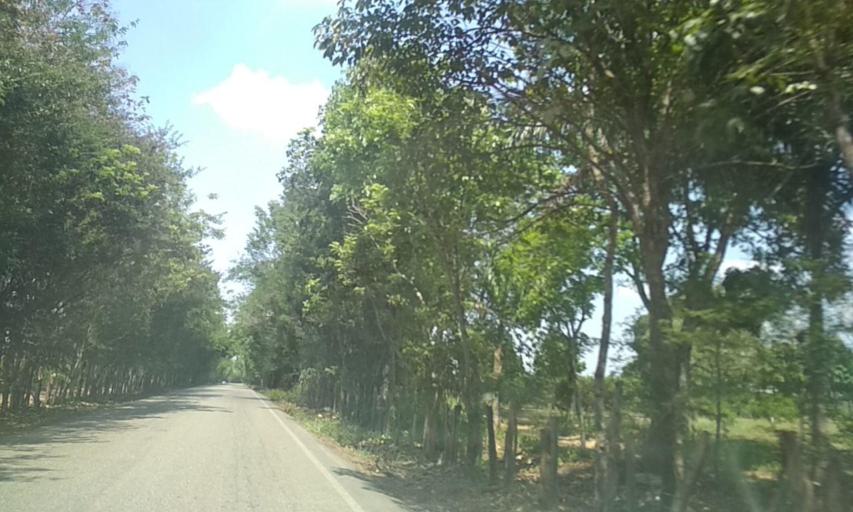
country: MX
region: Tabasco
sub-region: Huimanguillo
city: Paso de la Mina 2da. Seccion (Barrial)
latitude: 17.7746
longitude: -93.6419
